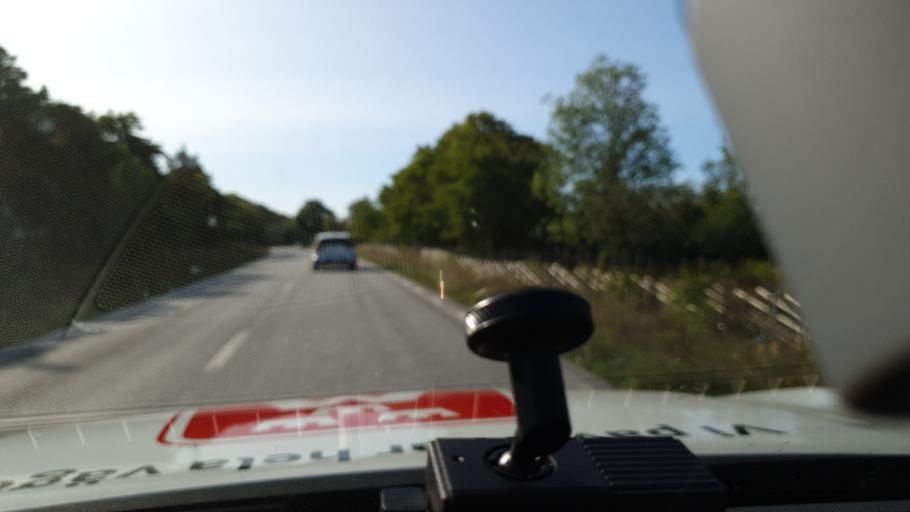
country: SE
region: Gotland
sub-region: Gotland
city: Klintehamn
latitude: 57.3472
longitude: 18.1924
